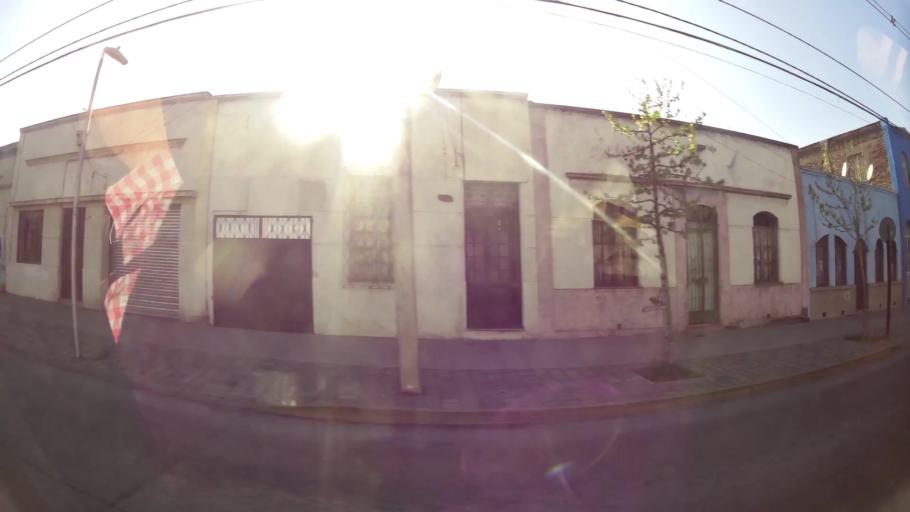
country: CL
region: Santiago Metropolitan
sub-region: Provincia de Santiago
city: Santiago
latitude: -33.4636
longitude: -70.6352
